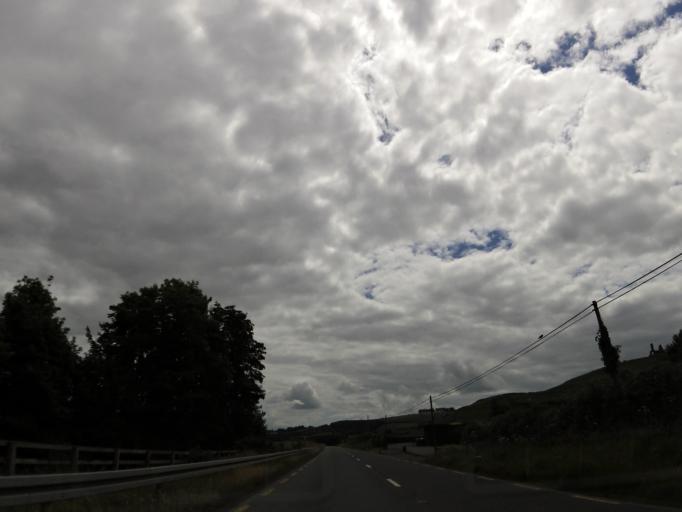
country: IE
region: Munster
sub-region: North Tipperary
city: Templemore
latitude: 52.7633
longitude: -8.0174
